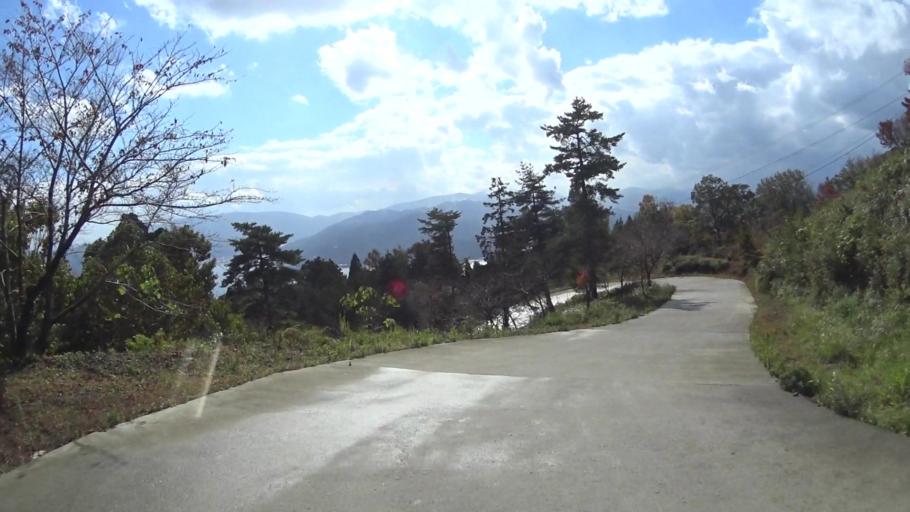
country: JP
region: Kyoto
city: Miyazu
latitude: 35.6036
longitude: 135.1935
